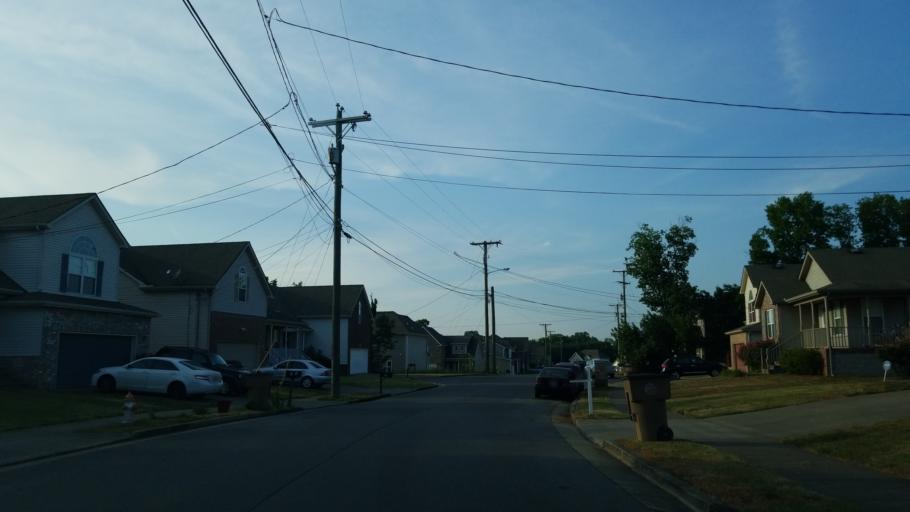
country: US
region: Tennessee
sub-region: Rutherford County
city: La Vergne
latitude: 36.0521
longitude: -86.5912
